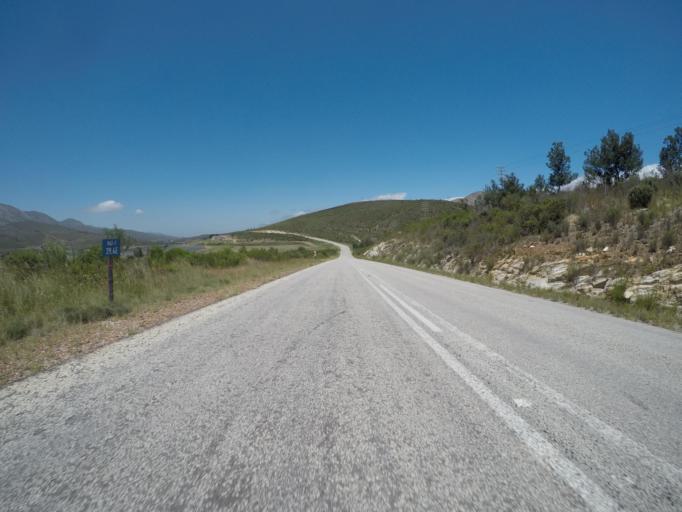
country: ZA
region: Eastern Cape
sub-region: Cacadu District Municipality
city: Kareedouw
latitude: -33.9079
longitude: 24.1579
